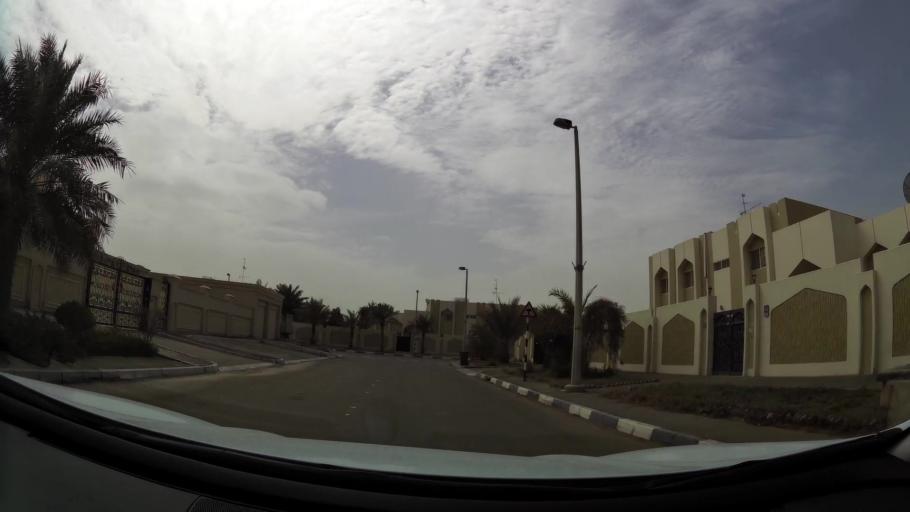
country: AE
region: Abu Dhabi
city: Abu Dhabi
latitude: 24.3957
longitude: 54.5026
